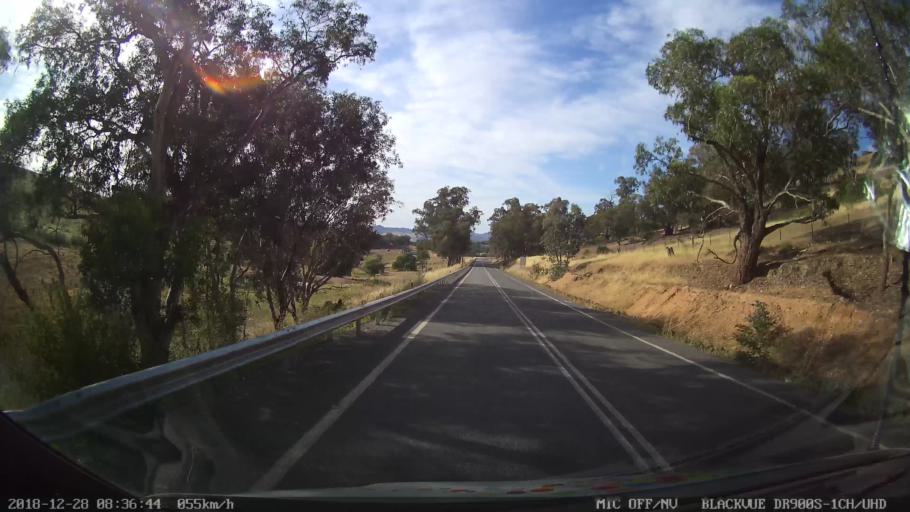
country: AU
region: New South Wales
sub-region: Blayney
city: Blayney
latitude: -33.9894
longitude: 149.3123
